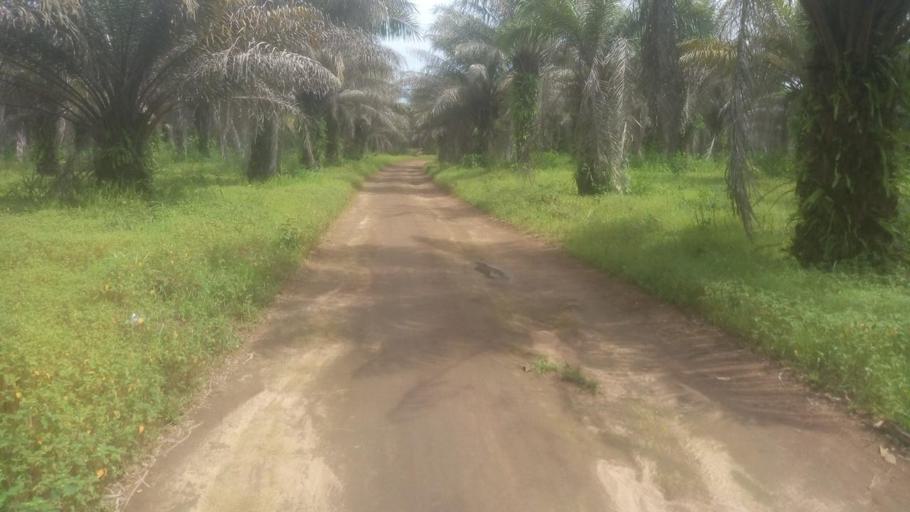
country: SL
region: Northern Province
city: Masoyila
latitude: 8.5909
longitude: -13.1903
